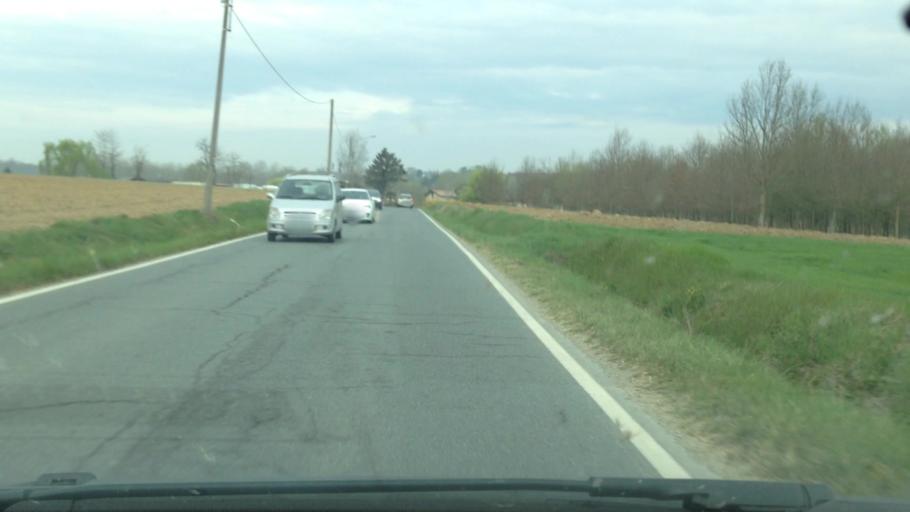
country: IT
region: Piedmont
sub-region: Provincia di Asti
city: Asti
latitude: 44.8950
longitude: 8.1722
